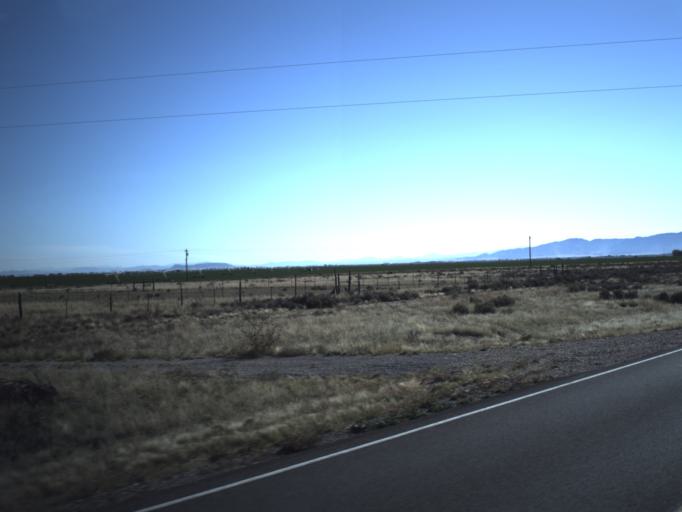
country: US
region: Utah
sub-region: Washington County
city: Enterprise
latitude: 37.7560
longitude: -113.7873
